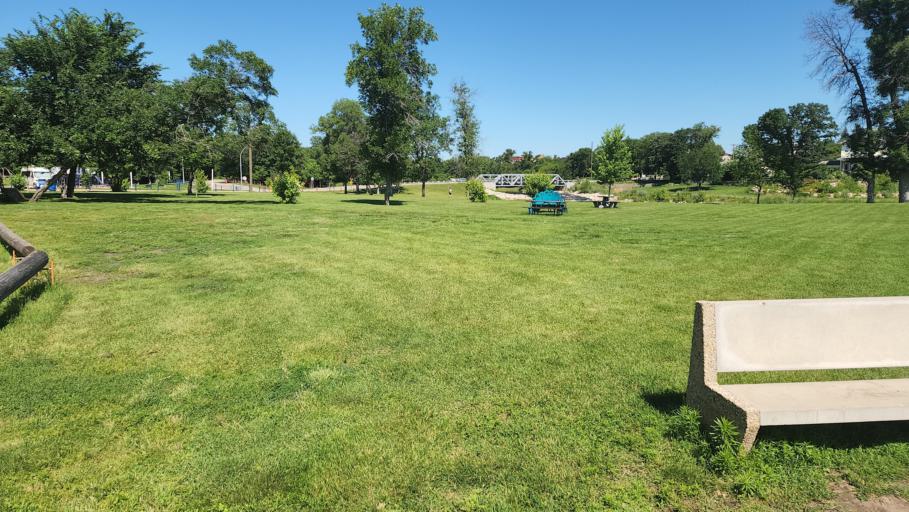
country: CA
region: Manitoba
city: Souris
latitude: 49.6131
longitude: -100.2570
